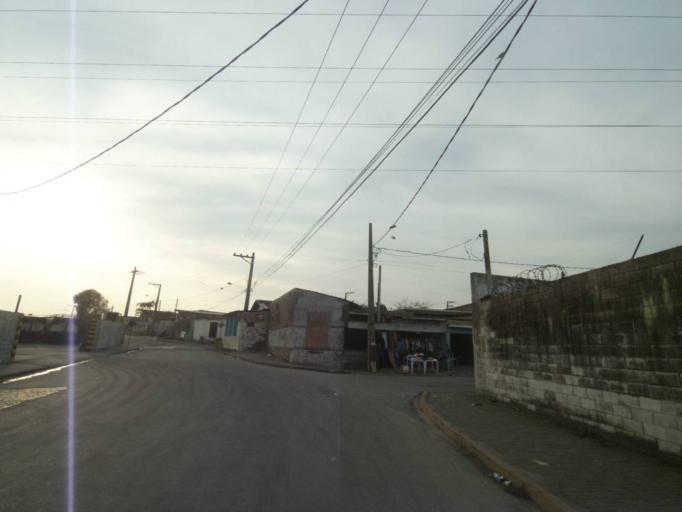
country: BR
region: Parana
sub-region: Paranagua
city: Paranagua
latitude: -25.5282
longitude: -48.5314
